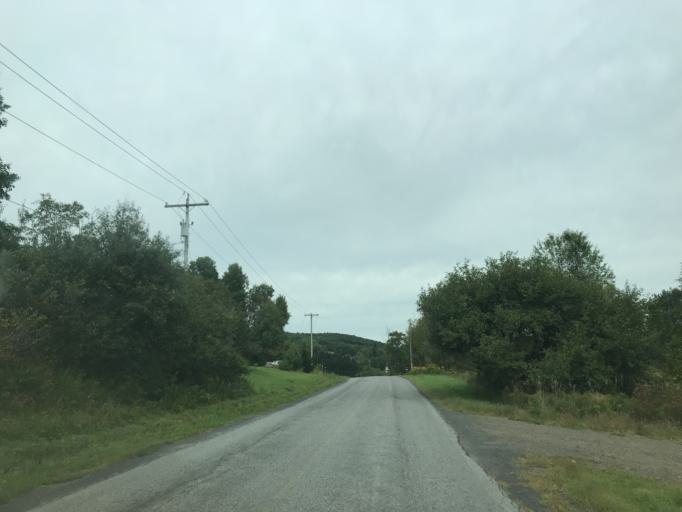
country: US
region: New York
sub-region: Otsego County
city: Worcester
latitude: 42.5601
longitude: -74.6673
